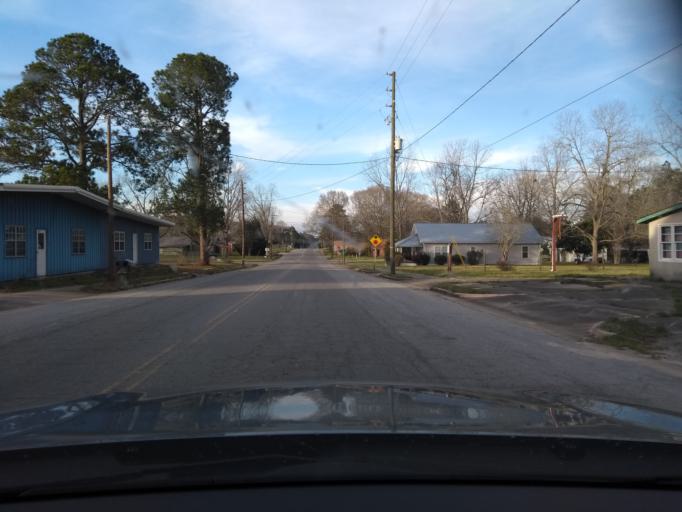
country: US
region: Georgia
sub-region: Bulloch County
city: Brooklet
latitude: 32.2644
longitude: -81.7611
